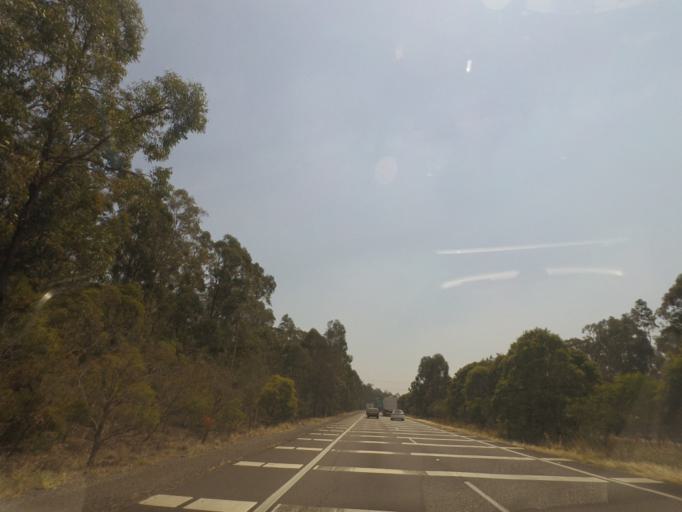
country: AU
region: New South Wales
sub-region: Newcastle
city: Beresfield
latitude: -32.8218
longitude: 151.6339
